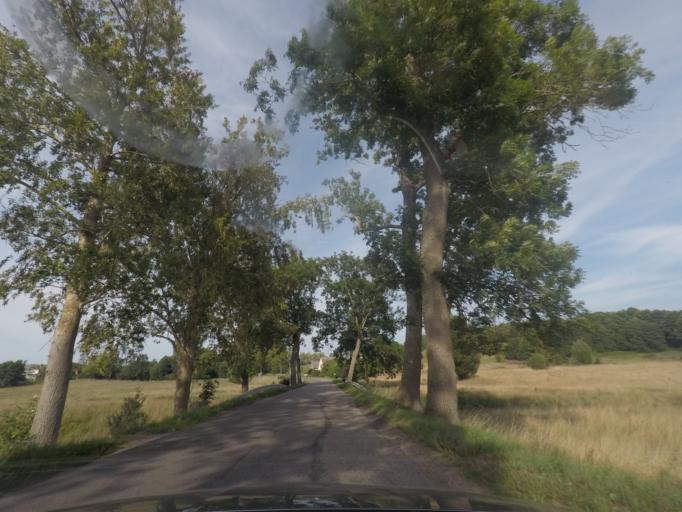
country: PL
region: Pomeranian Voivodeship
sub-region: Powiat slupski
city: Glowczyce
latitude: 54.6093
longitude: 17.3414
